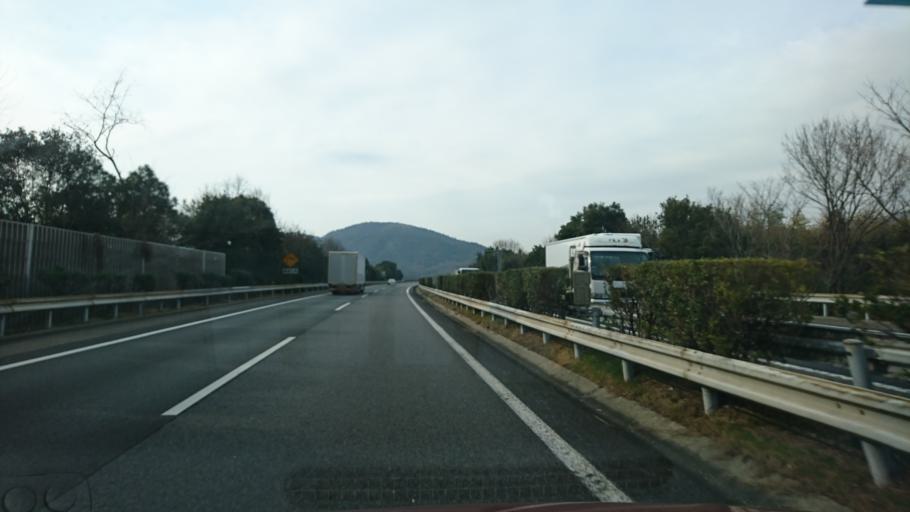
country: JP
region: Okayama
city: Kamogatacho-kamogata
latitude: 34.5393
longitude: 133.5638
